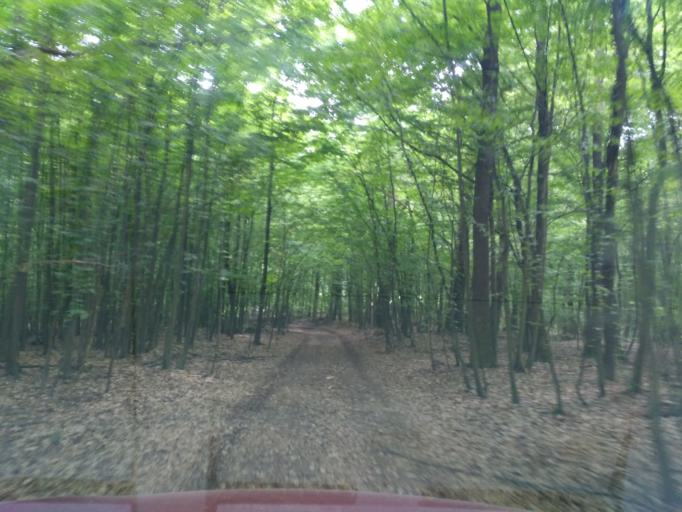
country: SK
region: Kosicky
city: Moldava nad Bodvou
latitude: 48.6572
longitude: 21.0405
